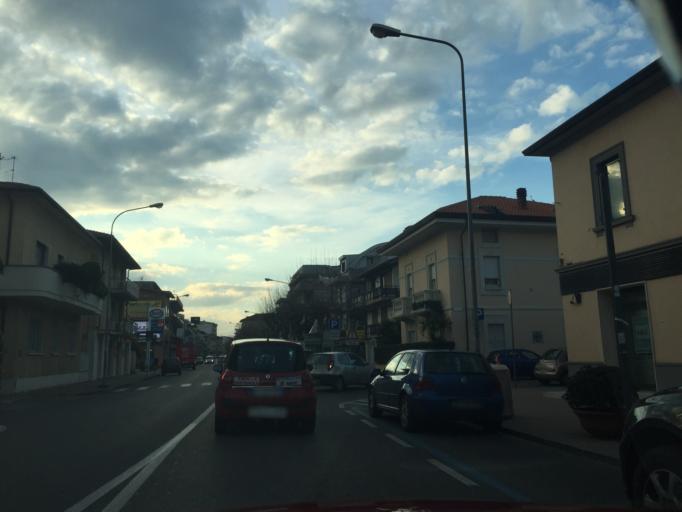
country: IT
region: Tuscany
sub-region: Provincia di Pistoia
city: Montecatini-Terme
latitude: 43.8804
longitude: 10.7798
